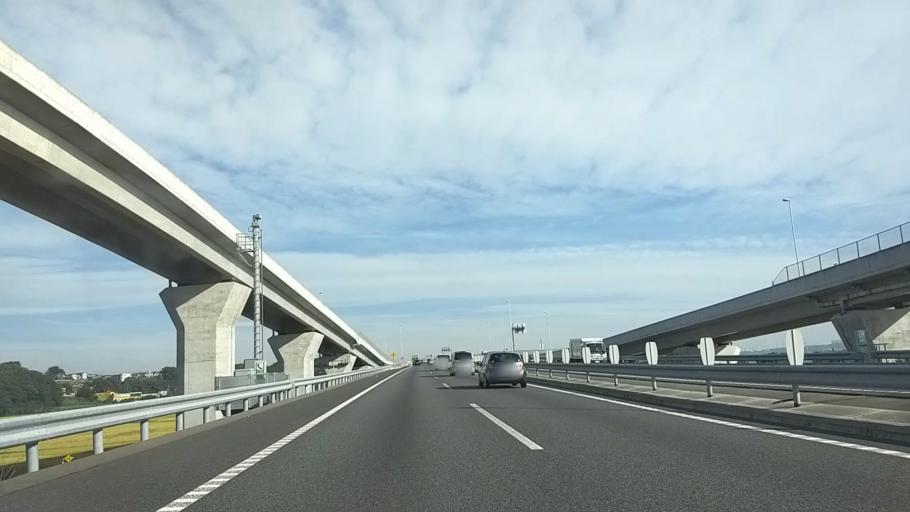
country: JP
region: Kanagawa
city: Zama
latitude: 35.4803
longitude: 139.3726
